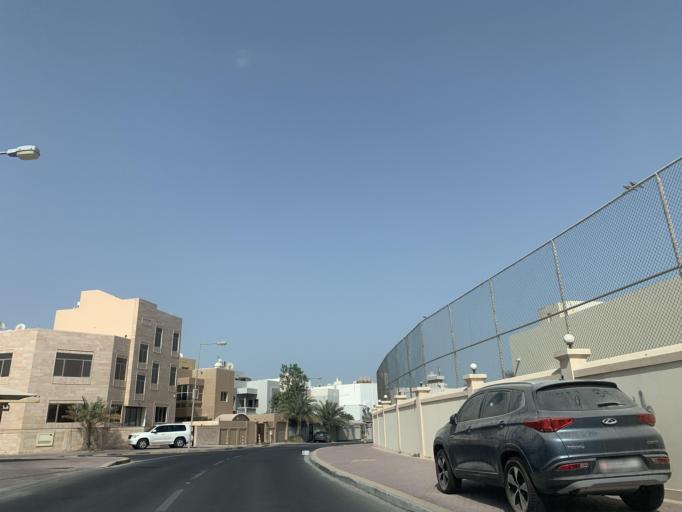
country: BH
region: Northern
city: Ar Rifa'
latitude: 26.1442
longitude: 50.5652
